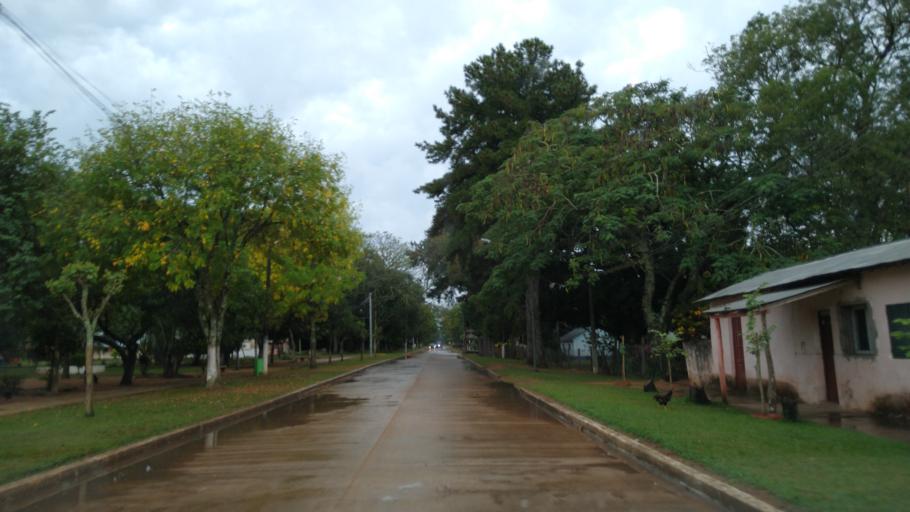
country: AR
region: Corrientes
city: Loreto
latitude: -27.7706
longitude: -57.2789
